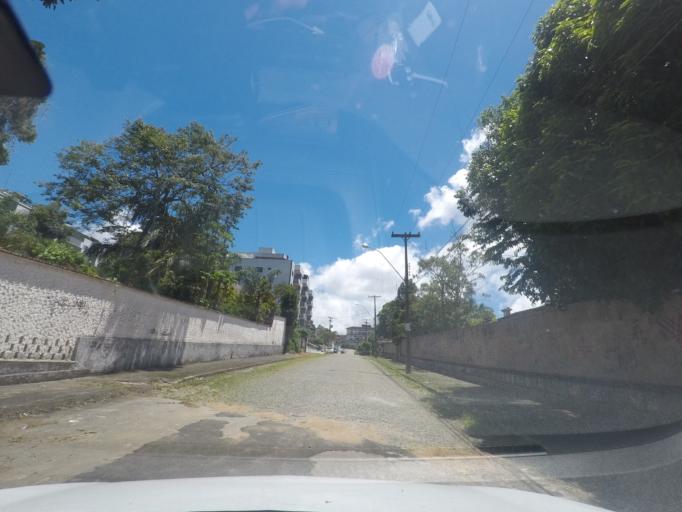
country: BR
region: Rio de Janeiro
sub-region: Teresopolis
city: Teresopolis
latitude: -22.4370
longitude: -42.9825
